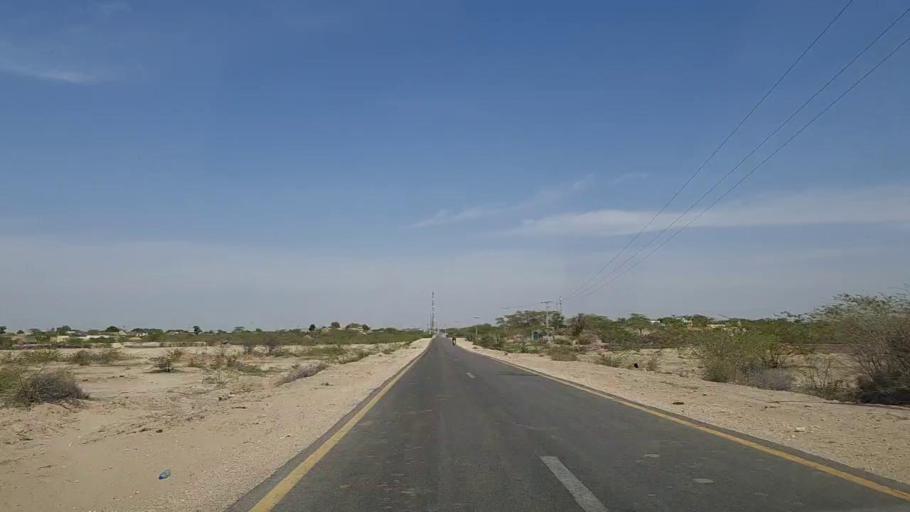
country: PK
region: Sindh
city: Mithi
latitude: 24.9691
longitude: 69.9137
